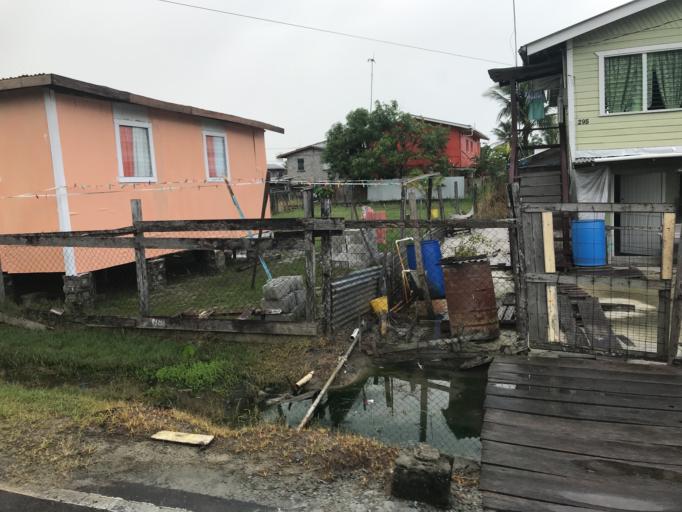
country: GY
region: Demerara-Mahaica
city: Georgetown
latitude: 6.8013
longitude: -58.1192
